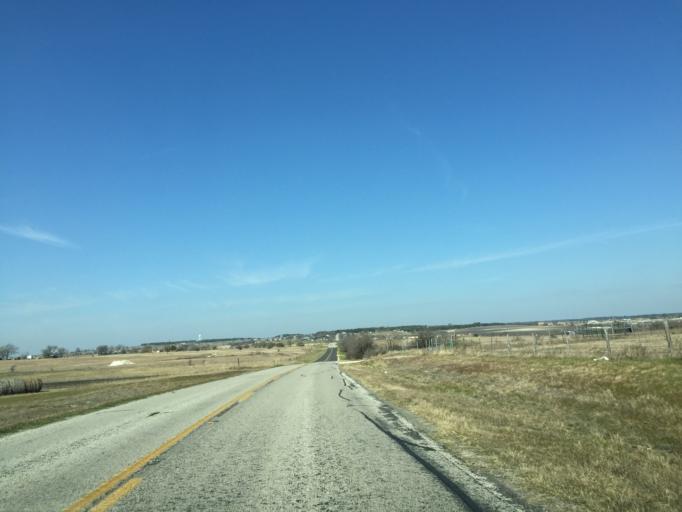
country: US
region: Texas
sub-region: Williamson County
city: Serenada
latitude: 30.7170
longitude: -97.5797
